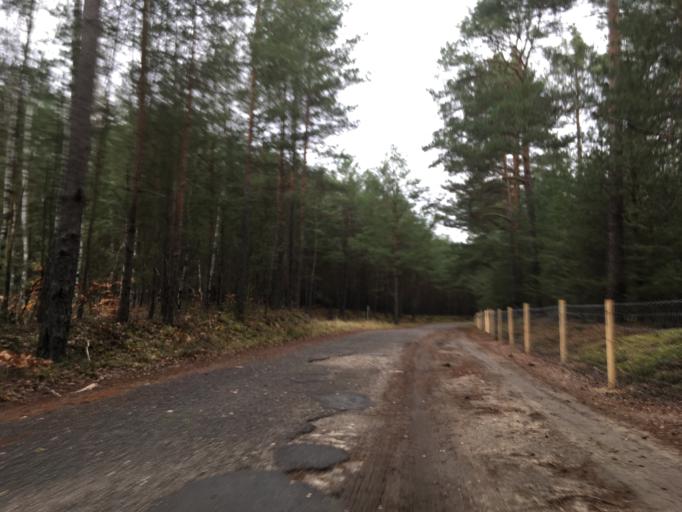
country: DE
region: Brandenburg
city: Jamlitz
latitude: 52.0590
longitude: 14.4805
